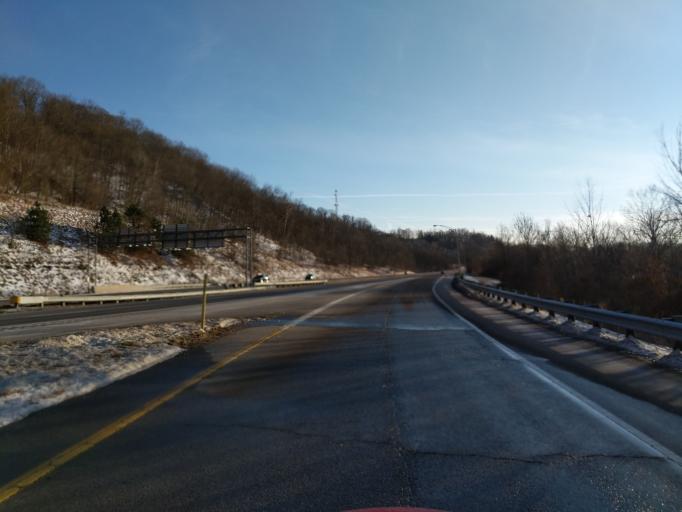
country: US
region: Ohio
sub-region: Athens County
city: Athens
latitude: 39.3235
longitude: -82.0892
